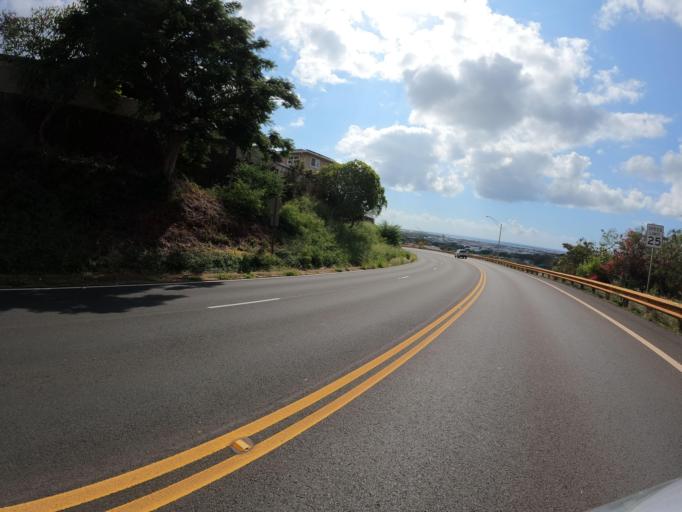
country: US
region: Hawaii
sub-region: Honolulu County
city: Halawa Heights
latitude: 21.3557
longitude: -157.8949
